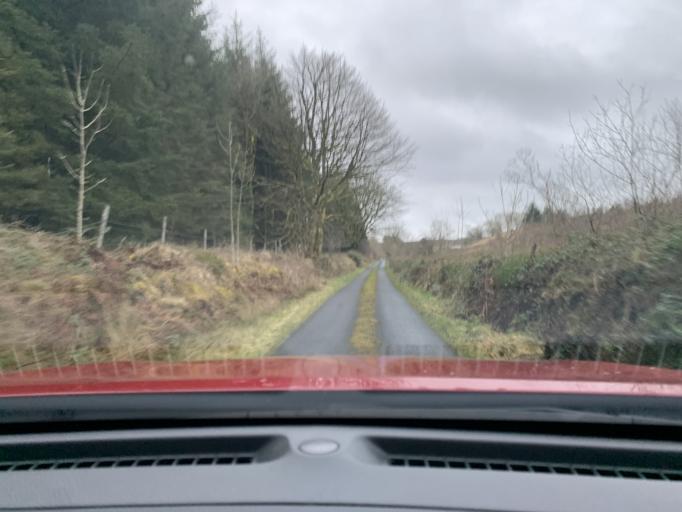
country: IE
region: Connaught
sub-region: Roscommon
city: Boyle
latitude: 54.0051
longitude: -8.3827
